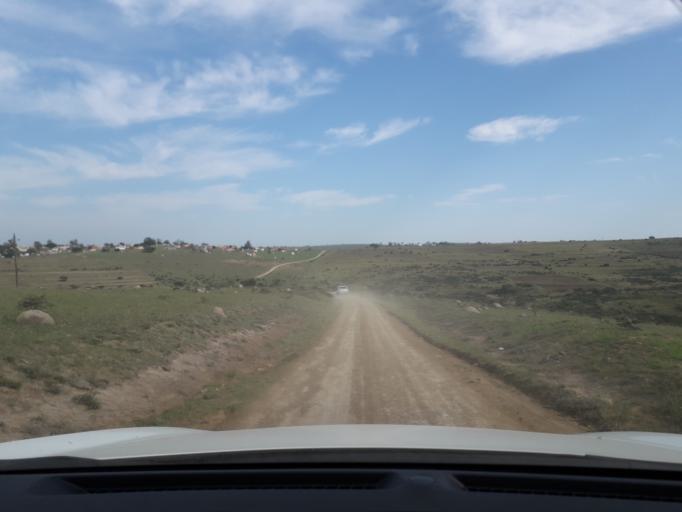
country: ZA
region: Eastern Cape
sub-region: Buffalo City Metropolitan Municipality
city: Bhisho
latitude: -32.9941
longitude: 27.3425
